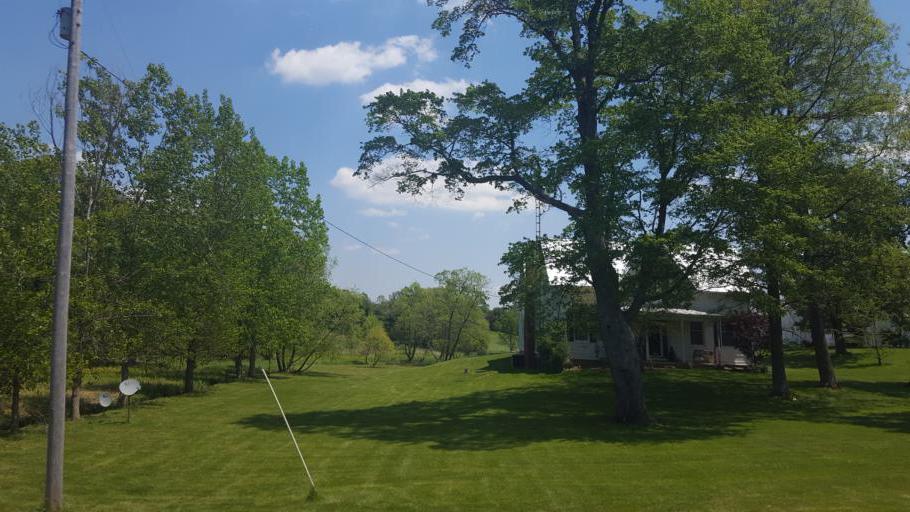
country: US
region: Ohio
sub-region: Knox County
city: Gambier
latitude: 40.3253
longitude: -82.4115
